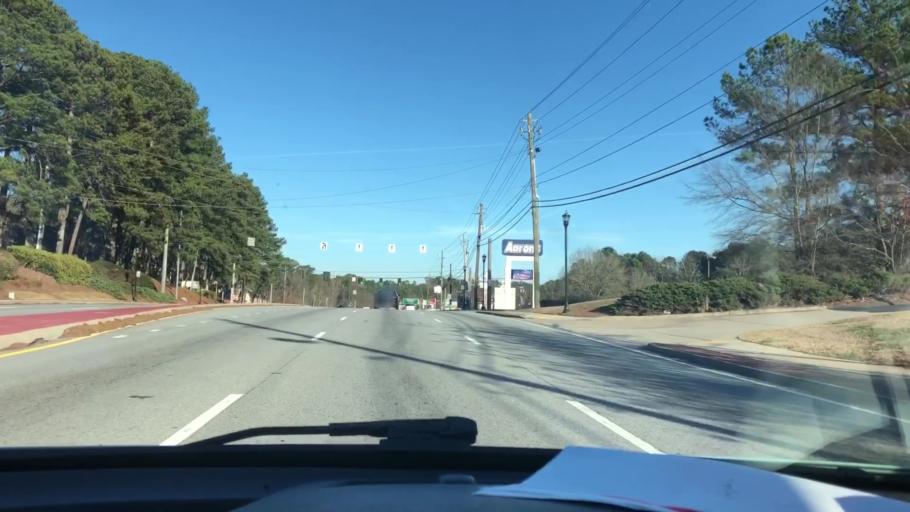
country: US
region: Georgia
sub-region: DeKalb County
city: Clarkston
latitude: 33.7994
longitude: -84.2184
